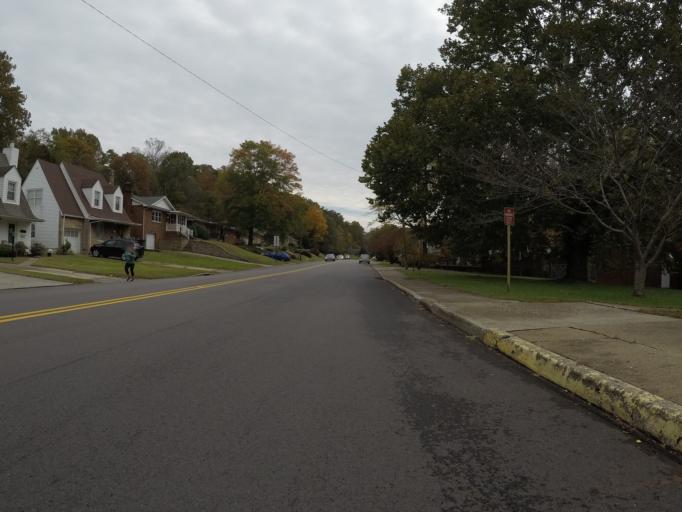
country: US
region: West Virginia
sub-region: Cabell County
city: Huntington
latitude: 38.4043
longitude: -82.4269
